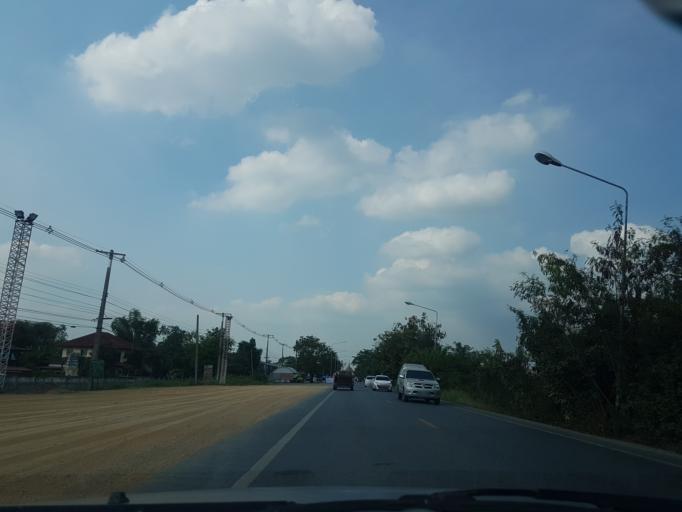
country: TH
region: Phra Nakhon Si Ayutthaya
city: Phachi
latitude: 14.3932
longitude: 100.7958
